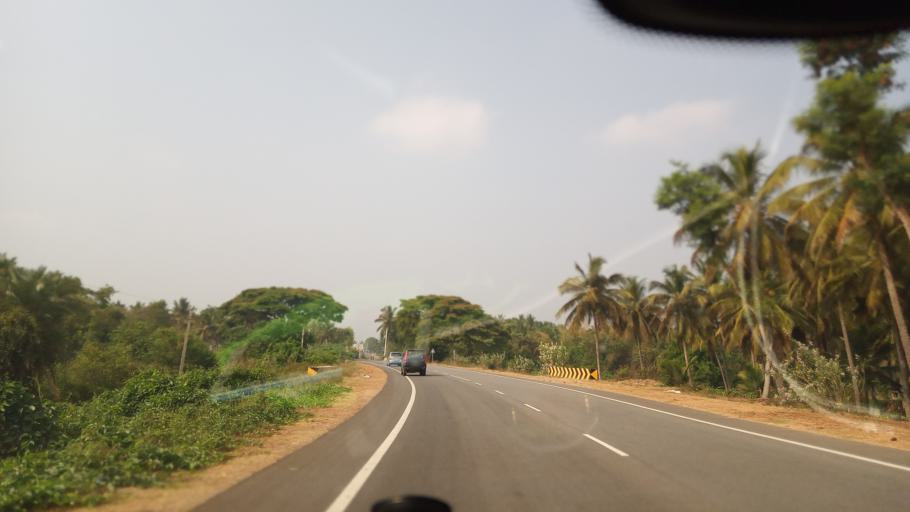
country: IN
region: Karnataka
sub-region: Mandya
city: Nagamangala
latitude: 12.7586
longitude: 76.7325
